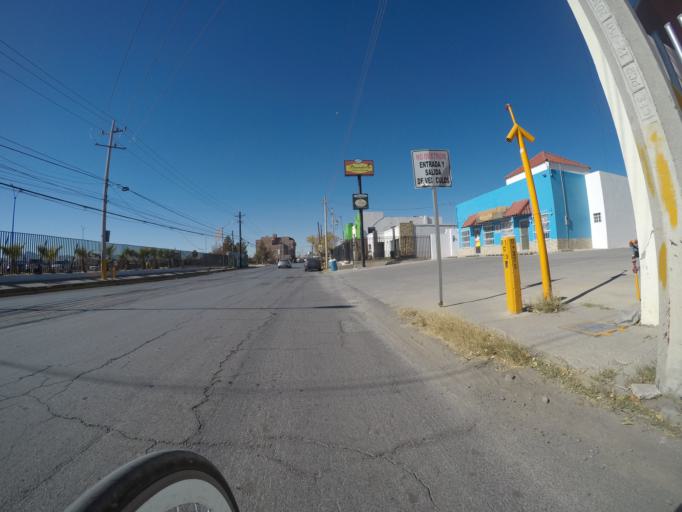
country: MX
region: Chihuahua
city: Ciudad Juarez
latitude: 31.7124
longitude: -106.4137
